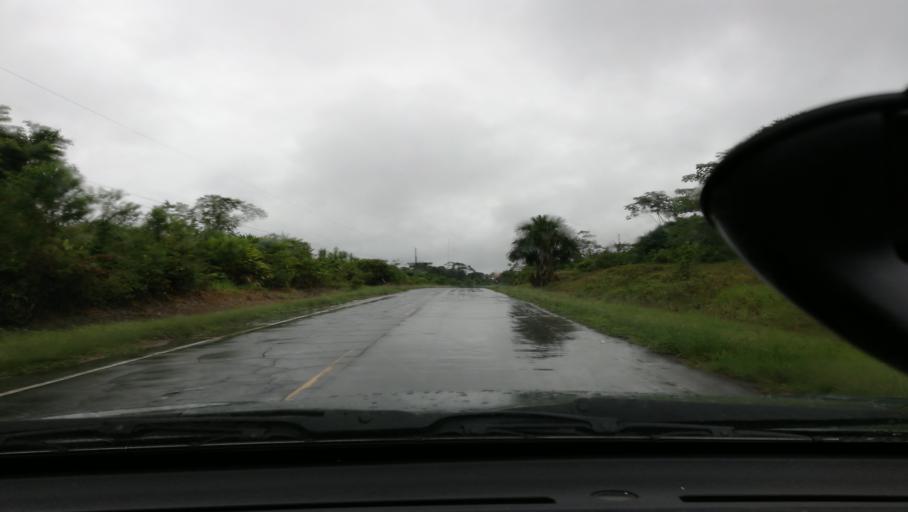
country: PE
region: Loreto
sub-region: Provincia de Maynas
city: San Juan
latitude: -4.1638
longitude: -73.4741
